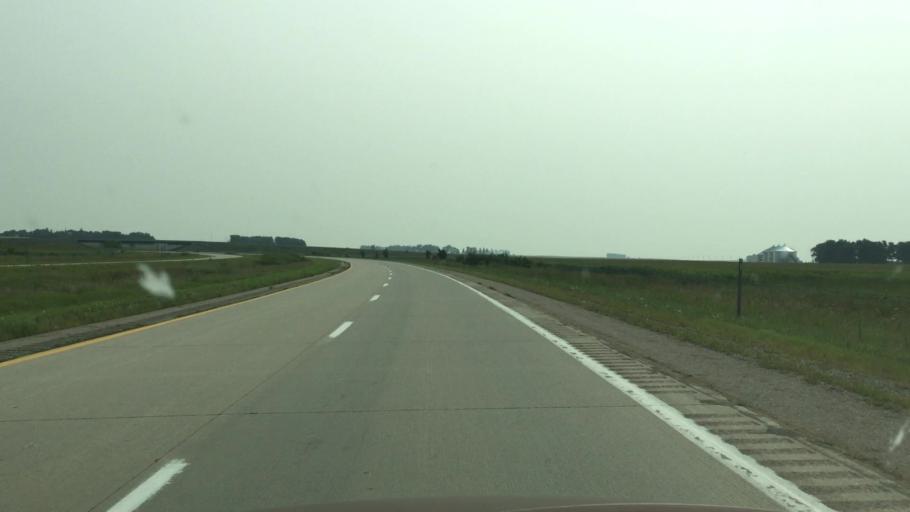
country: US
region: Iowa
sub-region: Osceola County
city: Sibley
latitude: 43.3844
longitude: -95.7307
